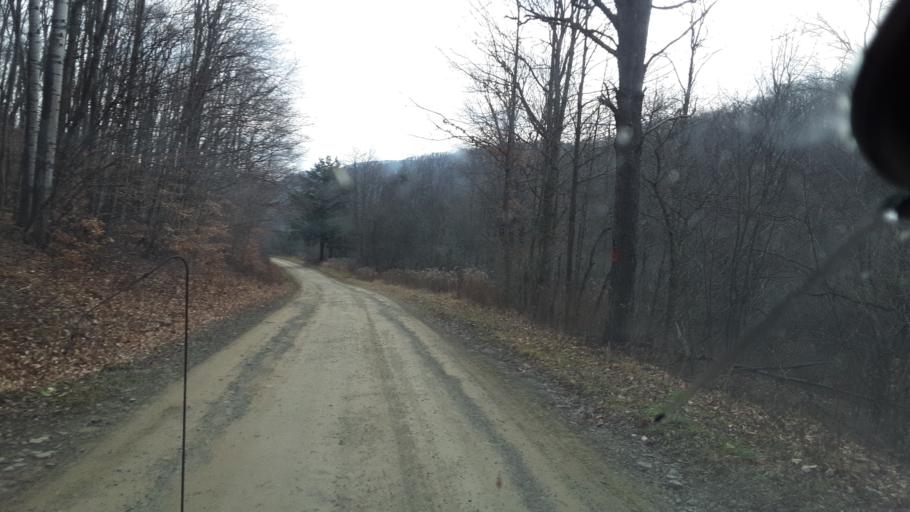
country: US
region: Pennsylvania
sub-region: Tioga County
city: Westfield
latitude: 41.9066
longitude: -77.7170
